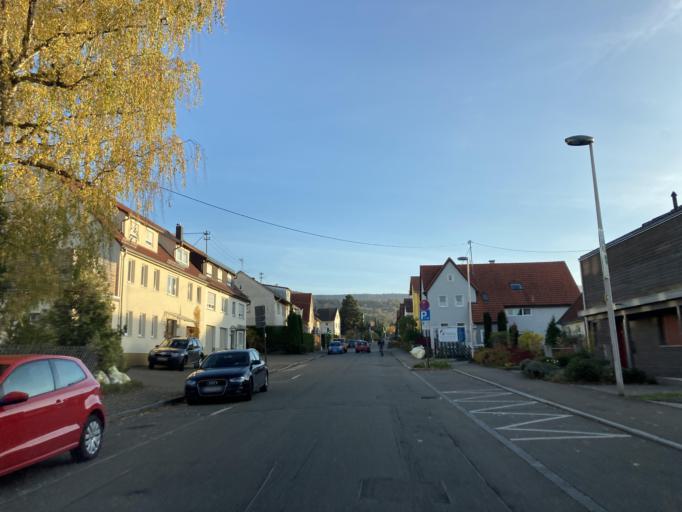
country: DE
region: Baden-Wuerttemberg
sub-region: Tuebingen Region
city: Mossingen
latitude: 48.4048
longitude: 9.0580
